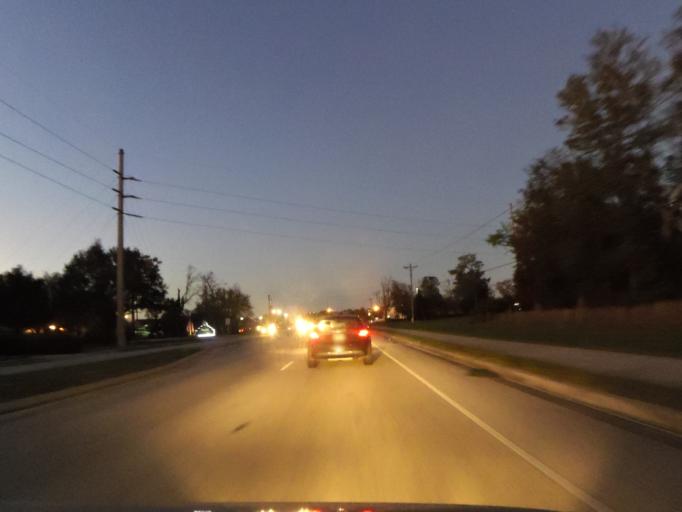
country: US
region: Florida
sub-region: Clay County
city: Lakeside
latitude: 30.1348
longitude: -81.7741
